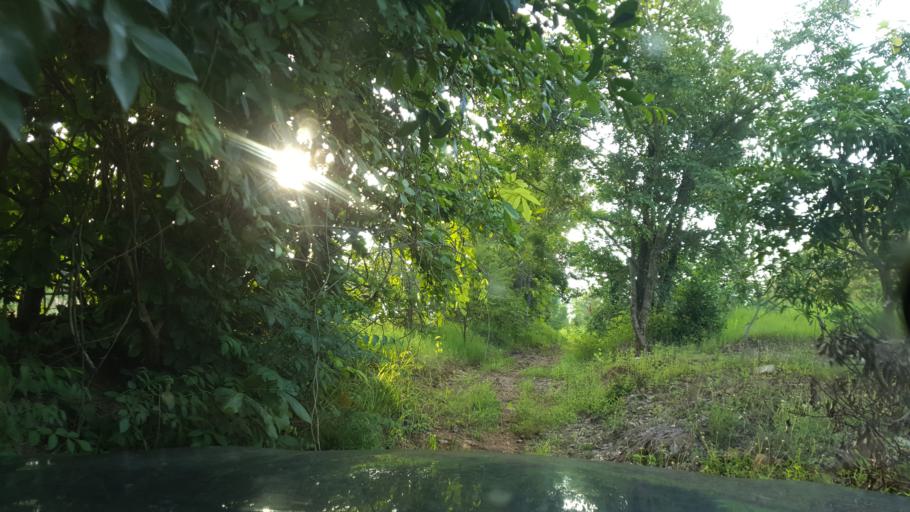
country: TH
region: Lamphun
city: Ban Thi
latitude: 18.6689
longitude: 99.1711
